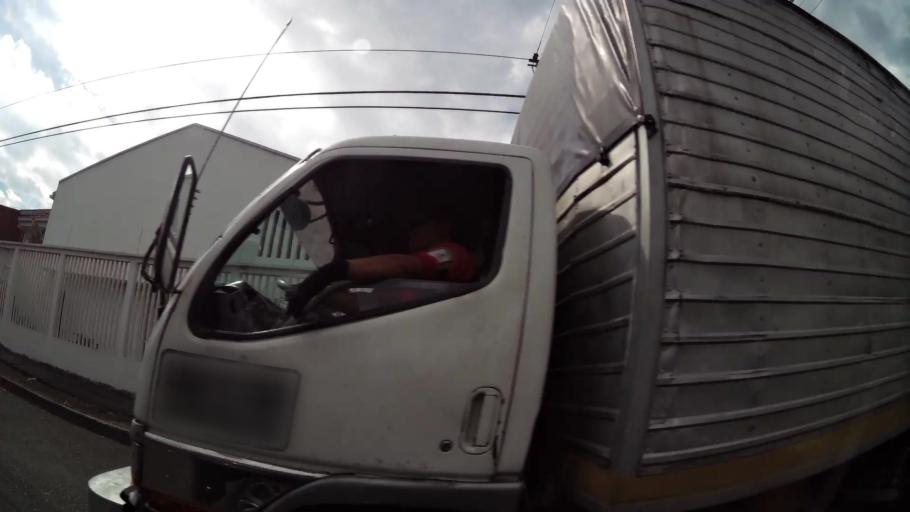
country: CO
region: Valle del Cauca
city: Cali
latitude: 3.4818
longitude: -76.5142
